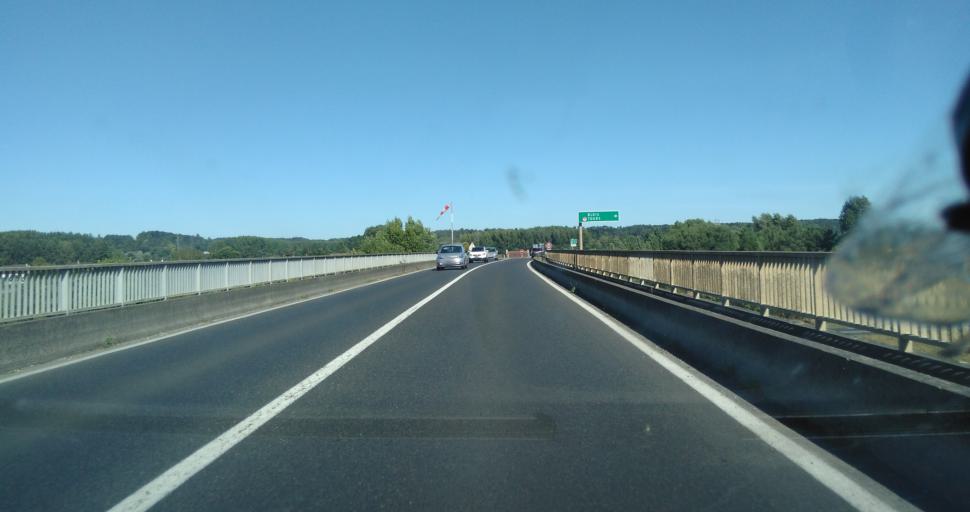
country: FR
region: Centre
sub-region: Departement d'Indre-et-Loire
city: Poce-sur-Cisse
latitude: 47.4301
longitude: 1.0082
